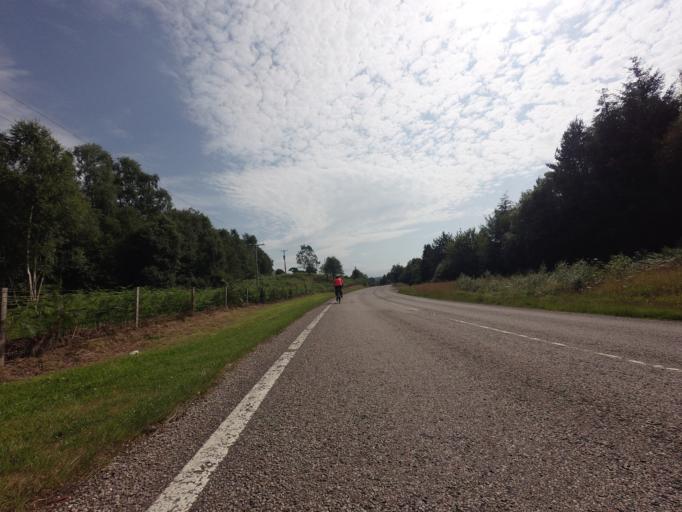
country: GB
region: Scotland
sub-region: Highland
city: Evanton
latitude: 57.9274
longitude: -4.4005
